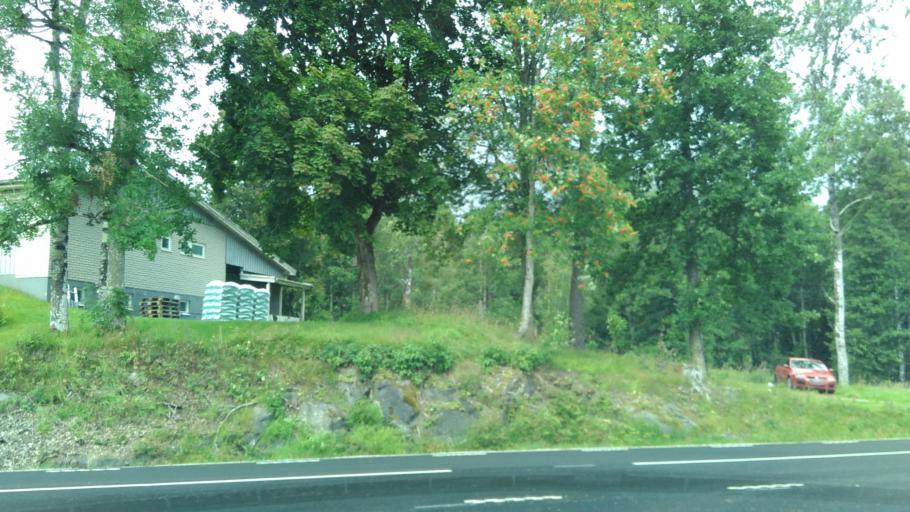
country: SE
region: Vaestra Goetaland
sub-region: Marks Kommun
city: Fritsla
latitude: 57.5904
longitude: 12.7495
